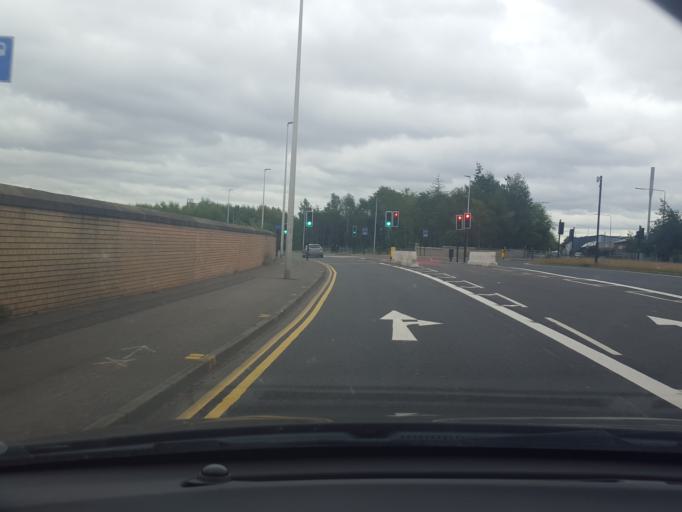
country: GB
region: Scotland
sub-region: Glasgow City
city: Glasgow
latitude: 55.8553
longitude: -4.2975
